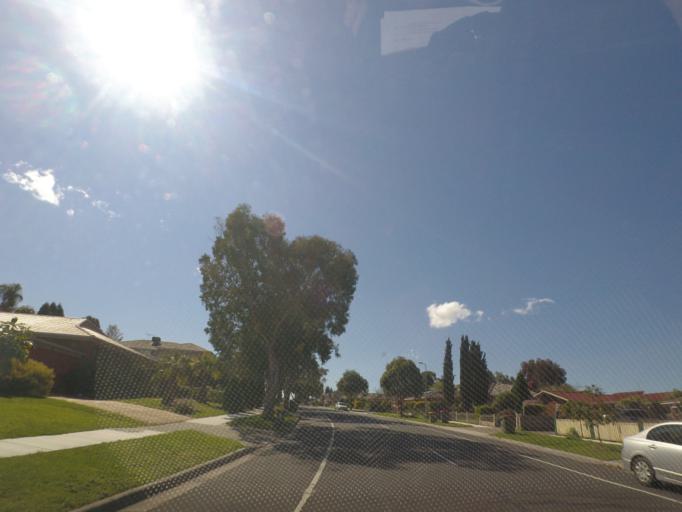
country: AU
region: Victoria
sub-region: Knox
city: Wantirna South
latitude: -37.8694
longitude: 145.2248
